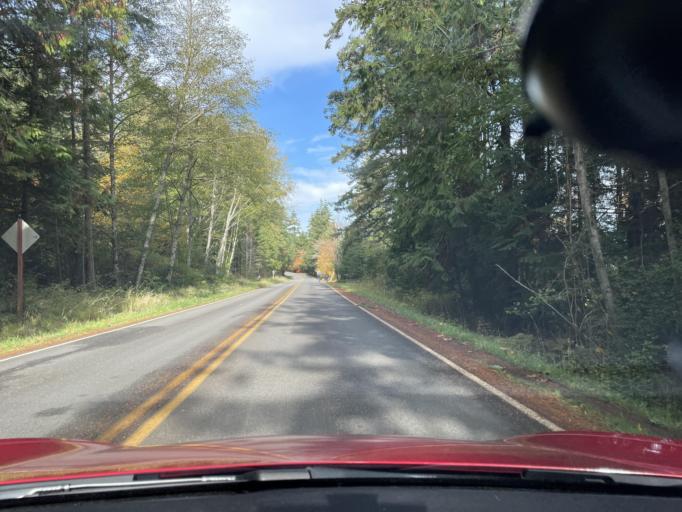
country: US
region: Washington
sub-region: San Juan County
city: Friday Harbor
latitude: 48.5288
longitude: -123.0050
